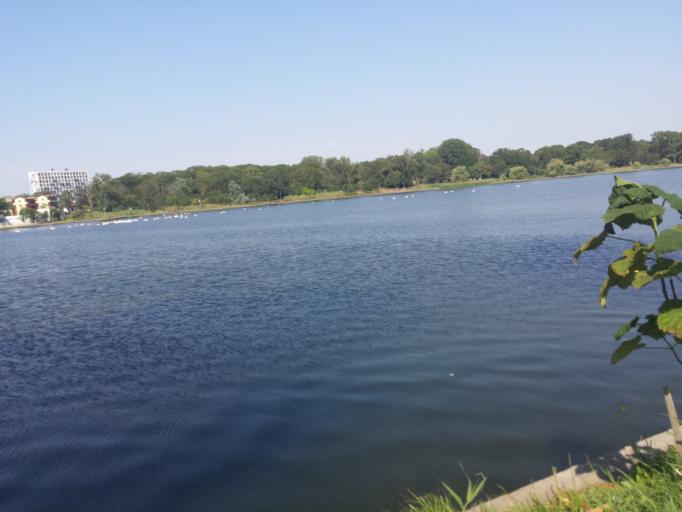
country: RO
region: Constanta
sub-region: Comuna Douazeci si Trei August
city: Douazeci si Trei August
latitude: 43.8618
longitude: 28.6058
